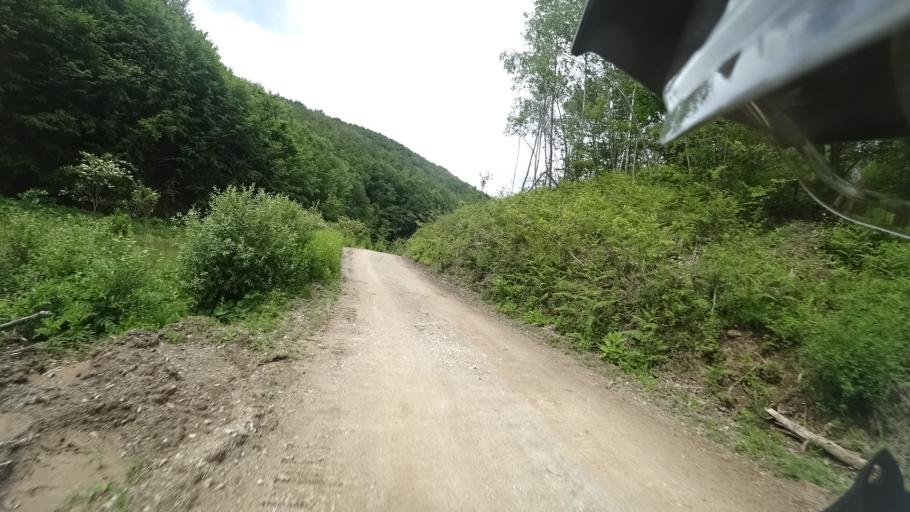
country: HR
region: Karlovacka
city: Vojnic
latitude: 45.2462
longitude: 15.6780
